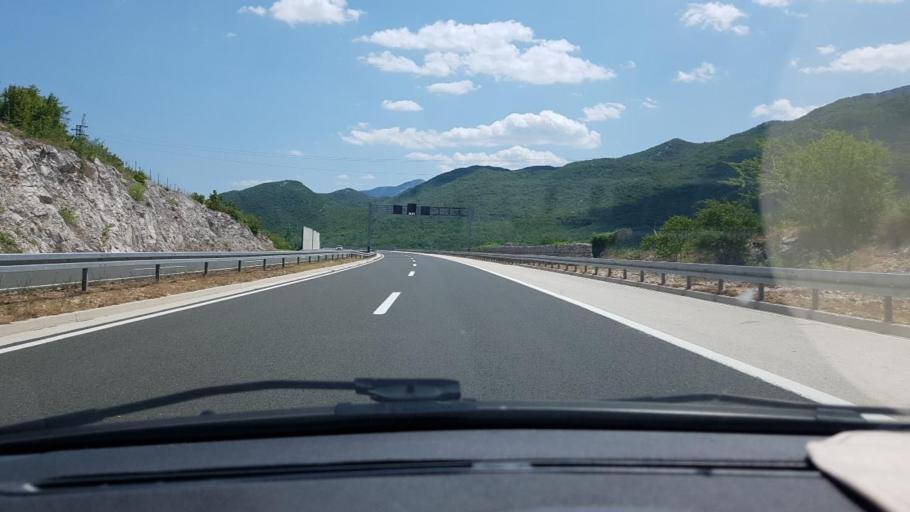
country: HR
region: Splitsko-Dalmatinska
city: Grubine
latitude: 43.3687
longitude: 17.0915
